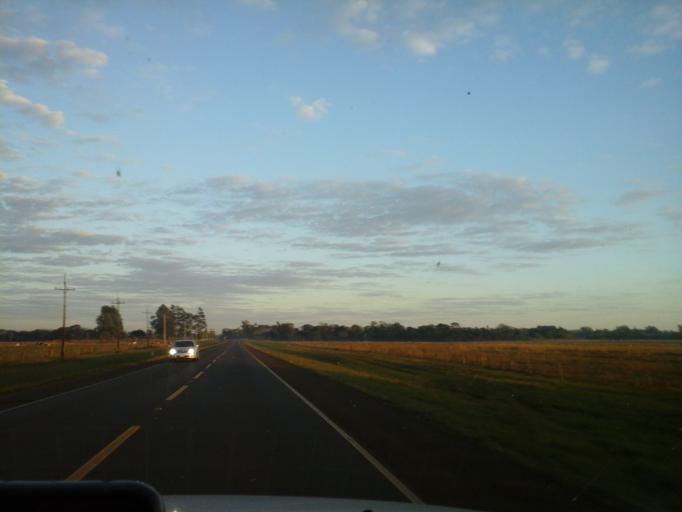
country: PY
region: Misiones
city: Santiago
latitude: -27.0400
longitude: -56.6642
